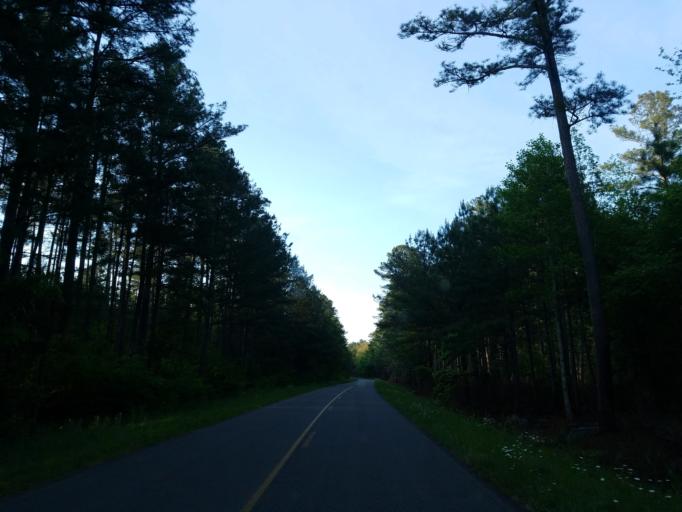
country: US
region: Georgia
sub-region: Gordon County
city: Calhoun
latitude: 34.6008
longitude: -85.0822
